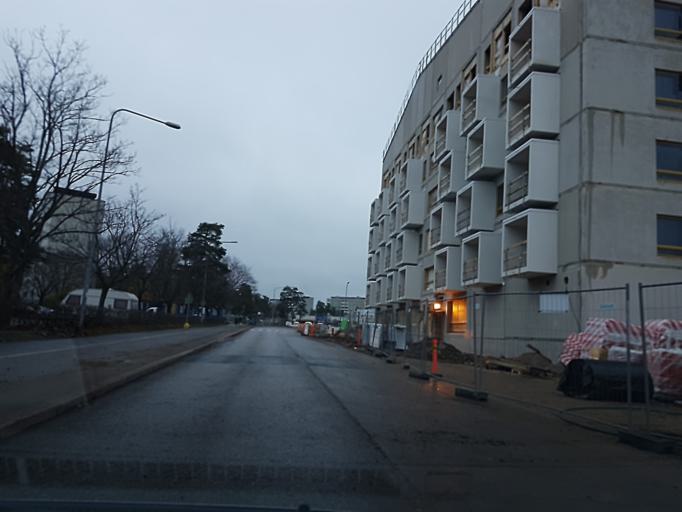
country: FI
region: Uusimaa
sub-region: Helsinki
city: Vantaa
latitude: 60.2350
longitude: 25.0797
